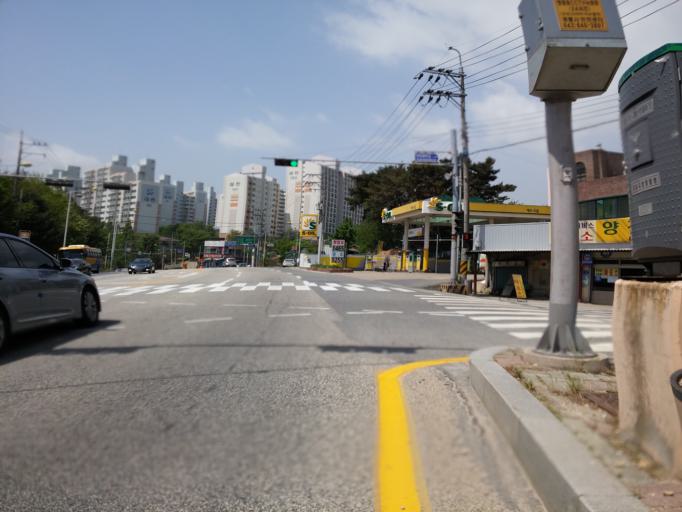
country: KR
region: Chungcheongnam-do
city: Nonsan
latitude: 36.2824
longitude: 127.2420
